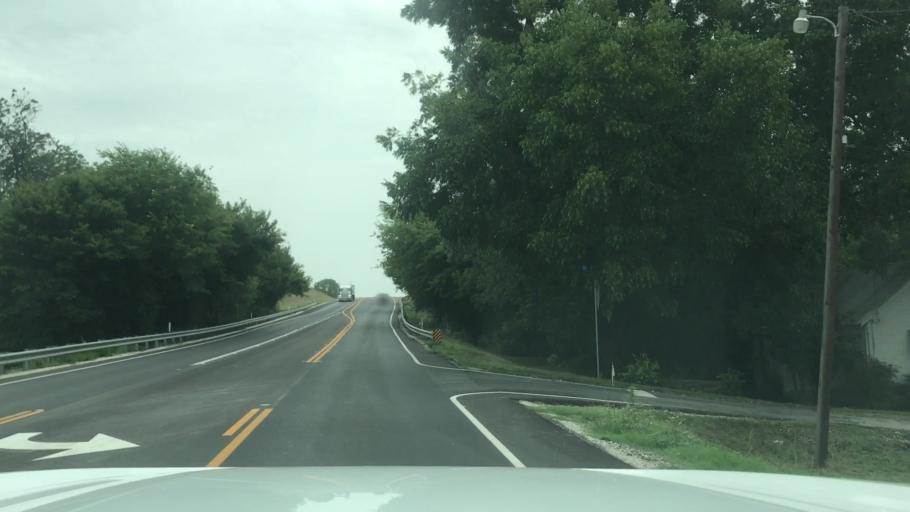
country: US
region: Texas
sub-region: Hamilton County
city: Hico
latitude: 31.9817
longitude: -98.0272
